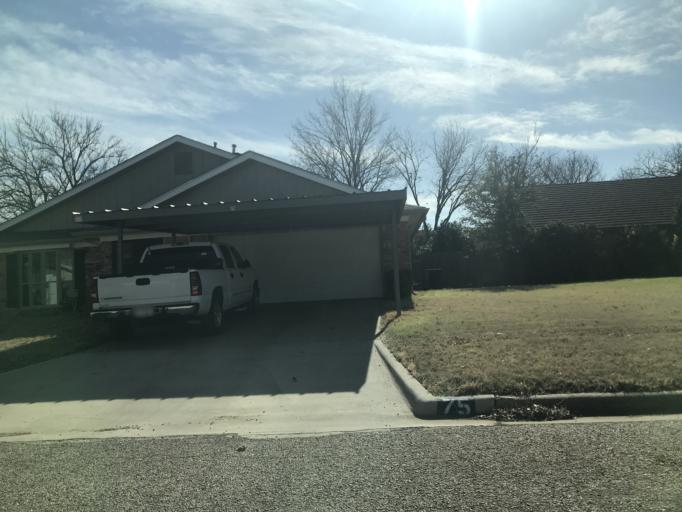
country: US
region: Texas
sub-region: Taylor County
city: Abilene
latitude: 32.4099
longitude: -99.7695
